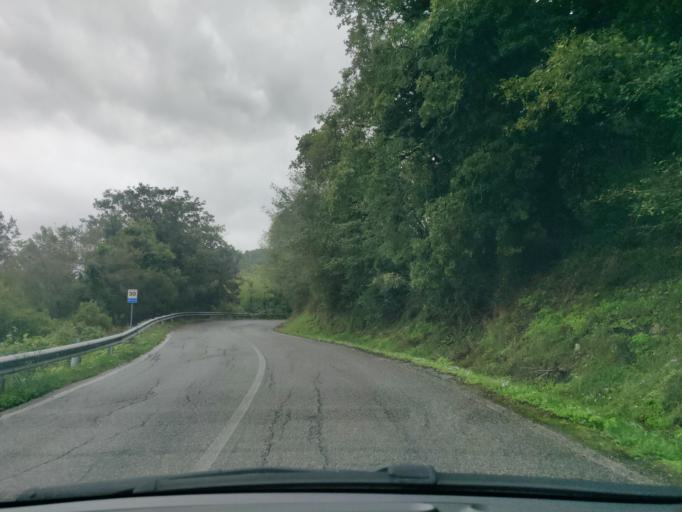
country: IT
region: Latium
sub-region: Citta metropolitana di Roma Capitale
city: Allumiere
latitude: 42.1452
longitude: 11.8811
